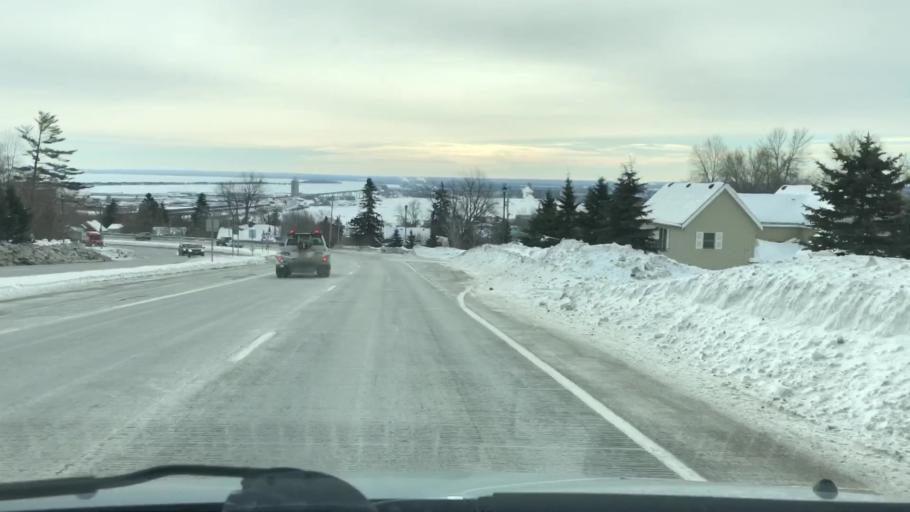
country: US
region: Minnesota
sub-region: Saint Louis County
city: Duluth
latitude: 46.7720
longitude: -92.1384
